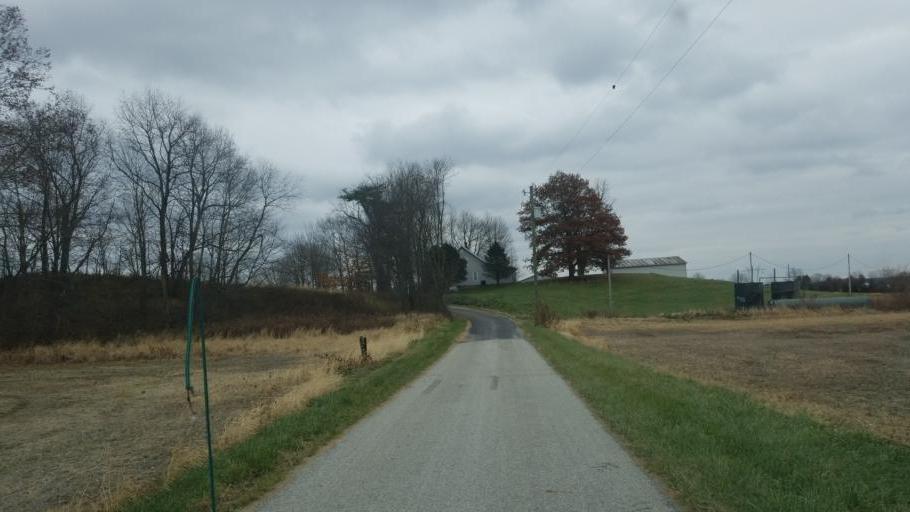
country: US
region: Ohio
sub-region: Knox County
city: Fredericktown
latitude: 40.5048
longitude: -82.5579
